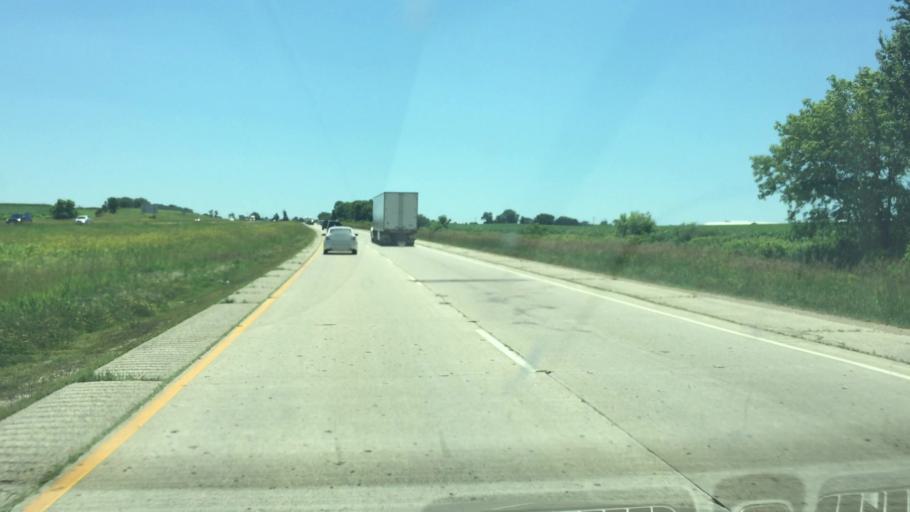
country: US
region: Wisconsin
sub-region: Dane County
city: Sun Prairie
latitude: 43.2256
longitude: -89.1610
